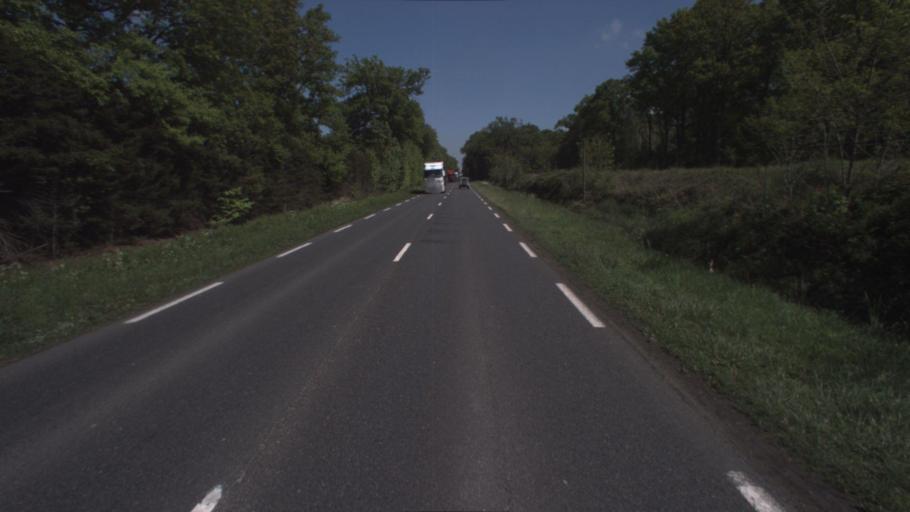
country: FR
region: Ile-de-France
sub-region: Departement de Seine-et-Marne
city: La Houssaye-en-Brie
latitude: 48.7952
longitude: 2.8701
